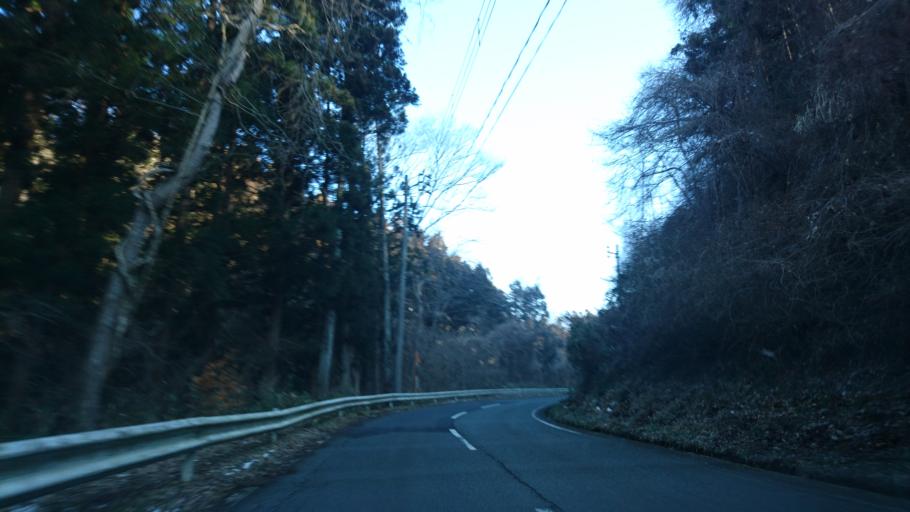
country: JP
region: Iwate
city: Ichinoseki
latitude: 38.9123
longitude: 141.2782
